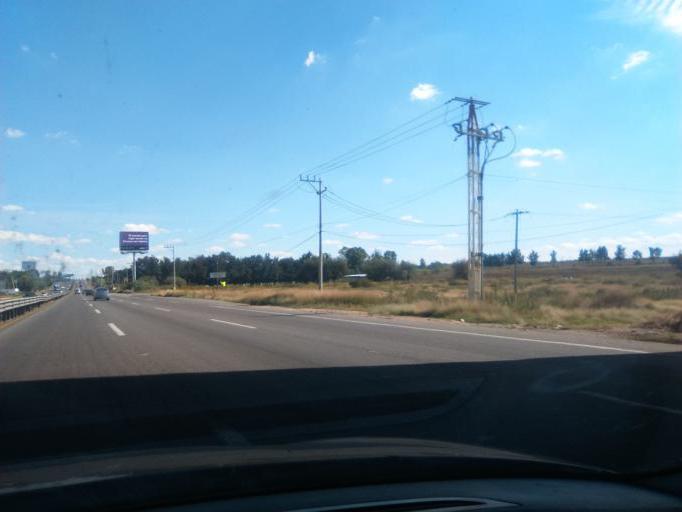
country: MX
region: Guanajuato
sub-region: Silao de la Victoria
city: San Antonio Texas
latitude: 20.9994
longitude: -101.5076
